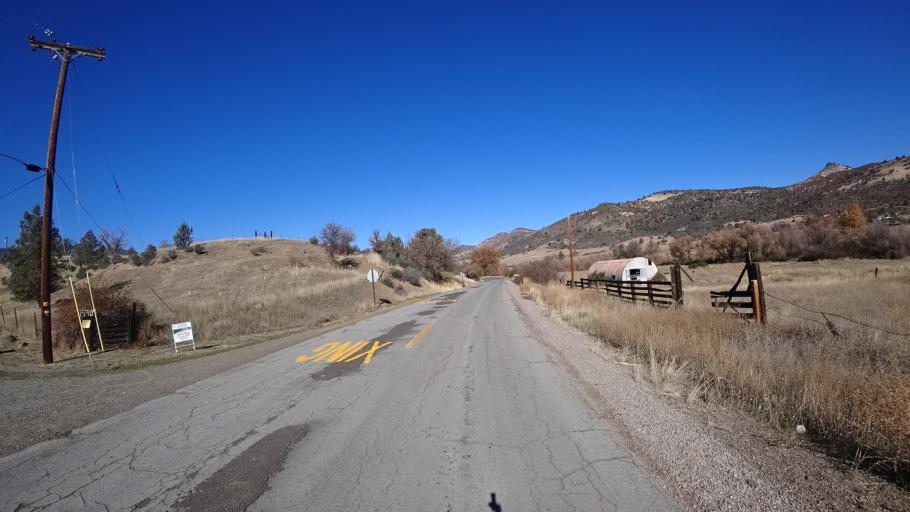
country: US
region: California
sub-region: Siskiyou County
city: Montague
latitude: 41.9130
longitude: -122.5621
